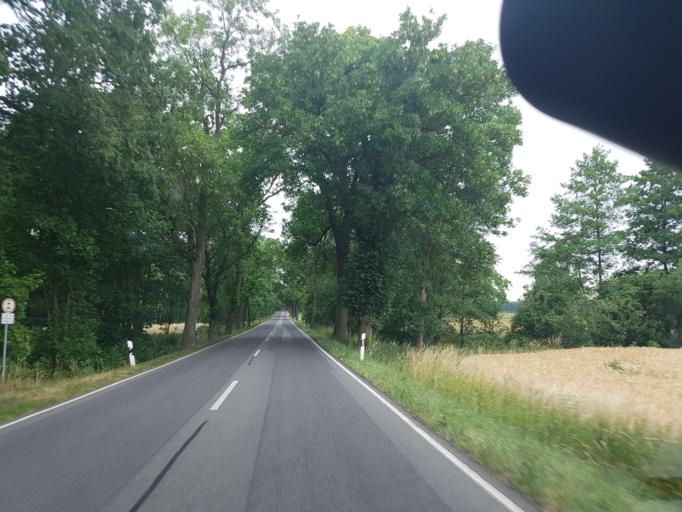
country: DE
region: Brandenburg
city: Lebusa
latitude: 51.8114
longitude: 13.4207
